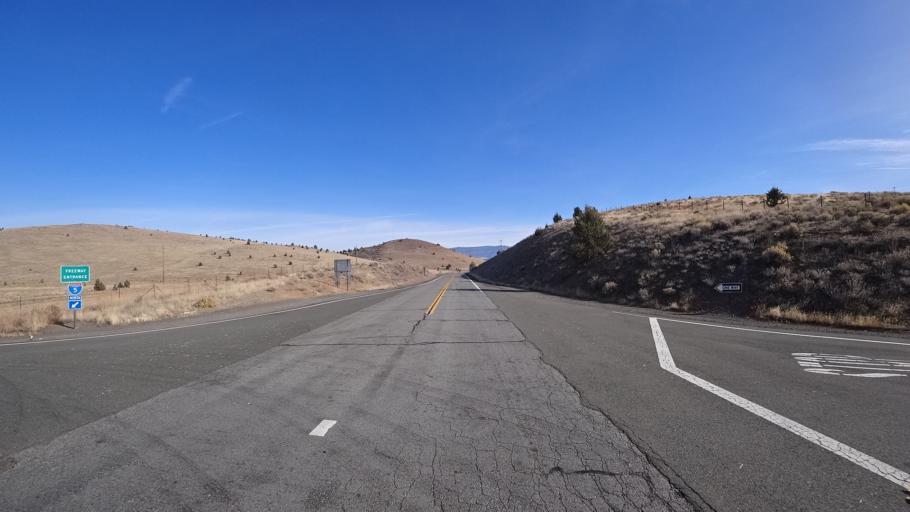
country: US
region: California
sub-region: Siskiyou County
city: Weed
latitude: 41.5528
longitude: -122.4841
